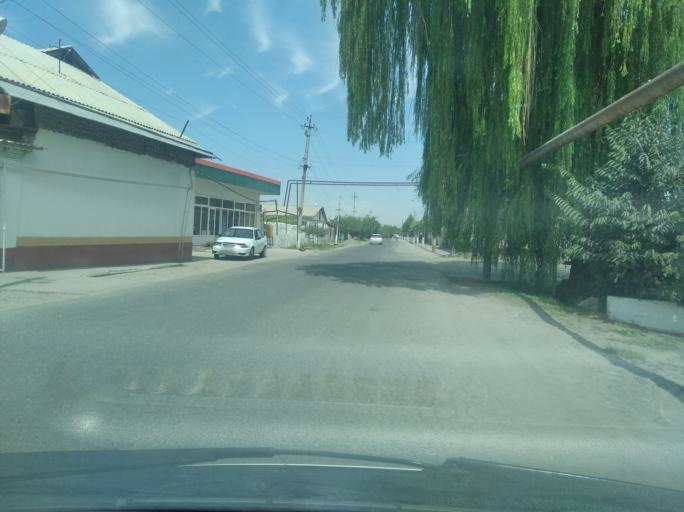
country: KG
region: Osh
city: Aravan
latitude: 40.6068
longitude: 72.4589
